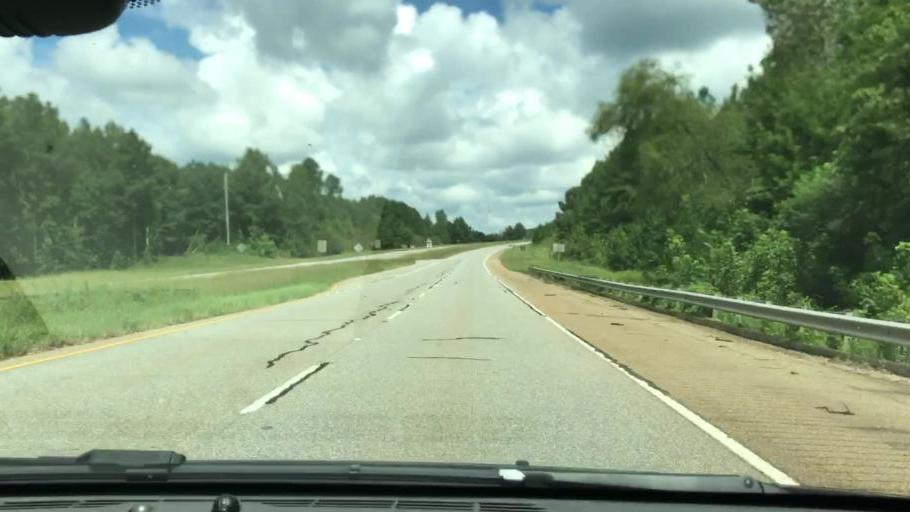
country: US
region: Georgia
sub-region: Stewart County
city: Lumpkin
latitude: 32.1036
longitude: -84.8121
